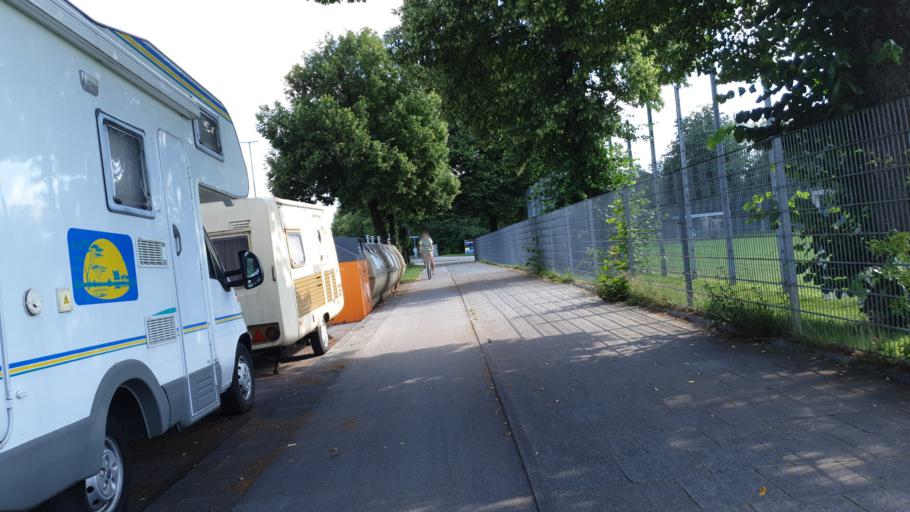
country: DE
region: Bavaria
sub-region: Upper Bavaria
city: Neubiberg
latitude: 48.0996
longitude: 11.6364
